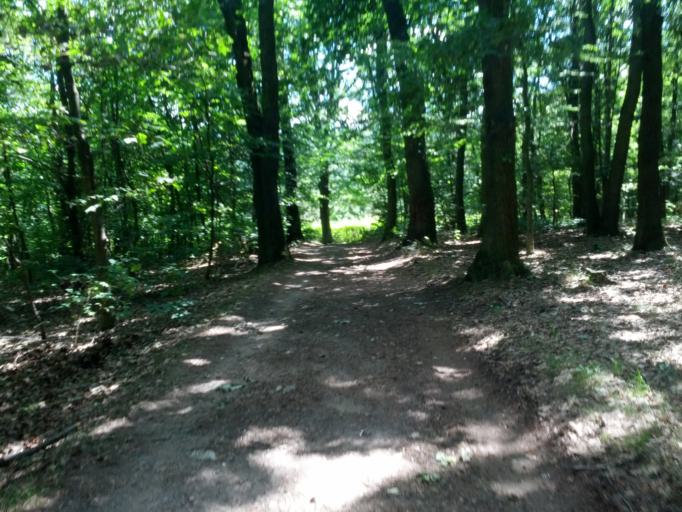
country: DE
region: Thuringia
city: Eisenach
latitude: 50.9635
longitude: 10.3289
